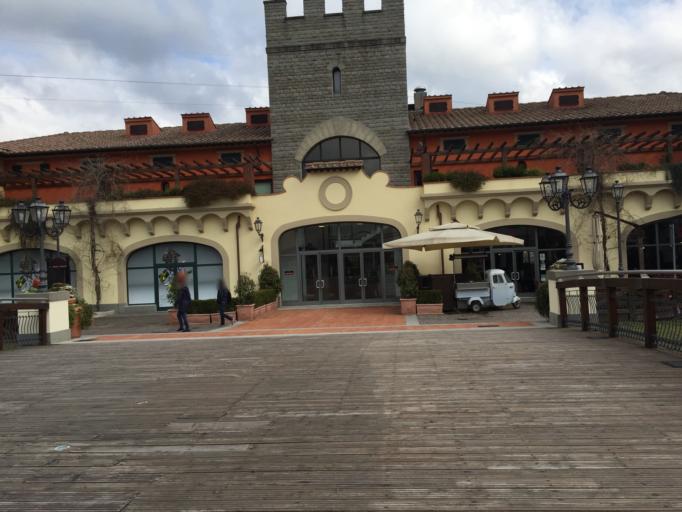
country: IT
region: Tuscany
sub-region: Province of Florence
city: Cavallina
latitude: 43.9848
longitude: 11.2156
